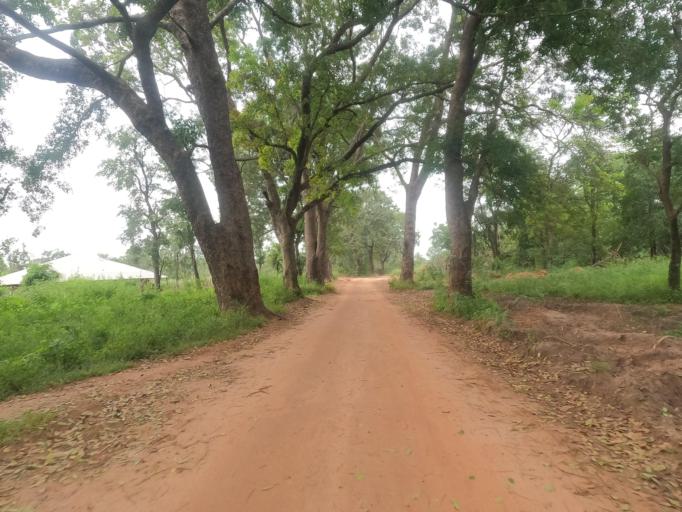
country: GW
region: Oio
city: Bissora
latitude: 12.4101
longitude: -15.5950
